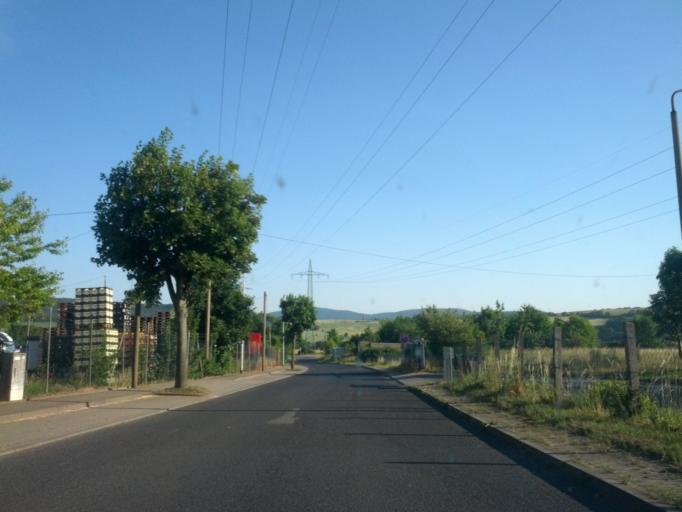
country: DE
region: Thuringia
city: Bischofroda
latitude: 50.9944
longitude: 10.3911
